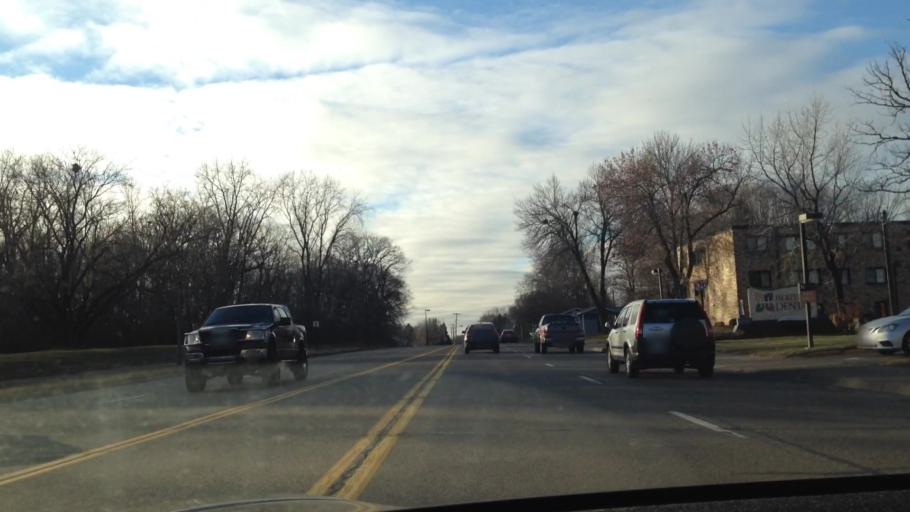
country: US
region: Minnesota
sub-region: Hennepin County
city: New Hope
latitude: 45.0330
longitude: -93.3866
